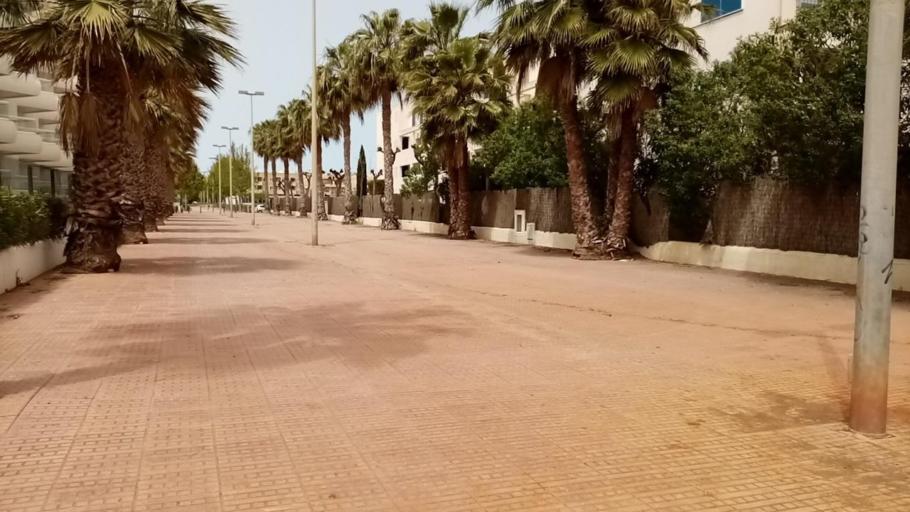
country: ES
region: Balearic Islands
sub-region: Illes Balears
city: Santa Eularia des Riu
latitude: 38.9879
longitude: 1.5459
